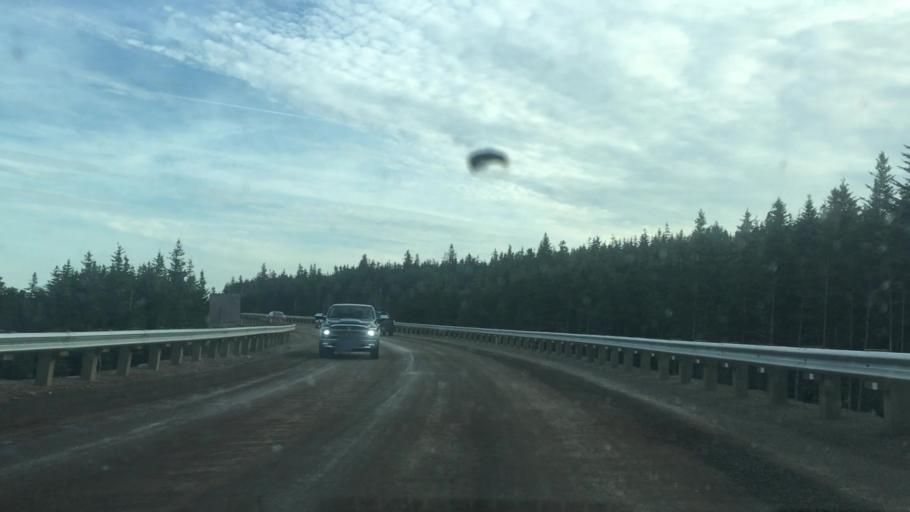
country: CA
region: Nova Scotia
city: Sydney Mines
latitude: 46.8064
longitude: -60.8443
